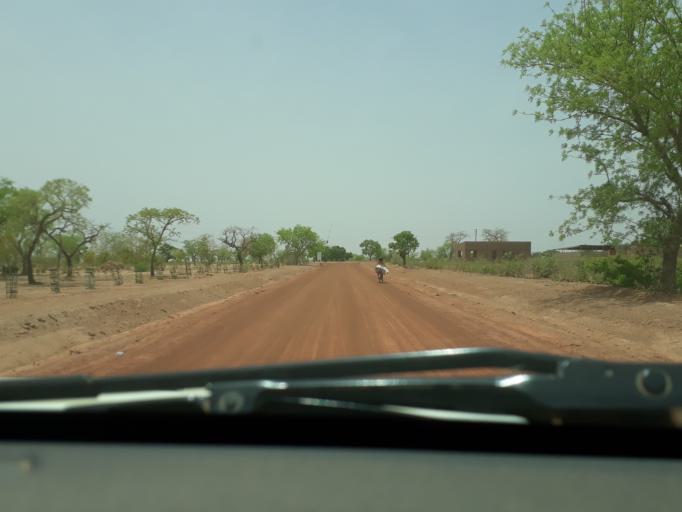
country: BF
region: Plateau-Central
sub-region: Province d'Oubritenga
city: Ziniare
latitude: 12.5792
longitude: -1.3326
